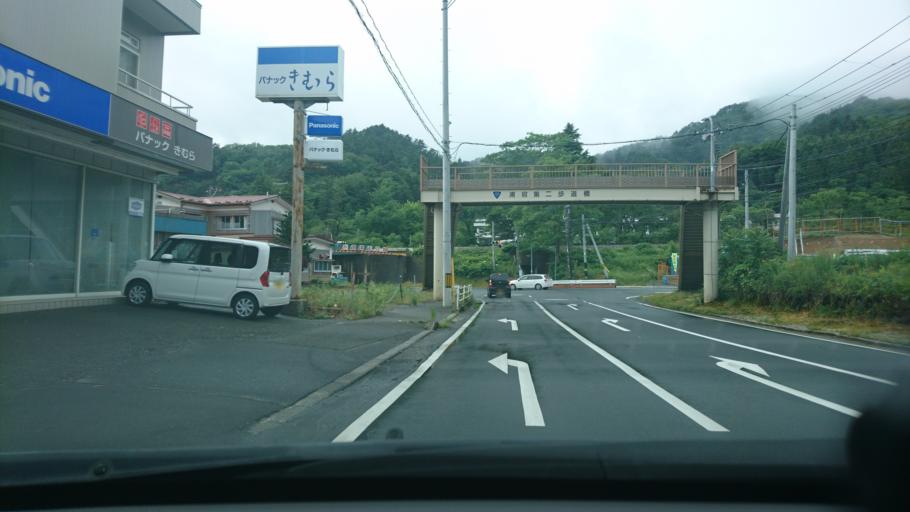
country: JP
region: Miyagi
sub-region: Oshika Gun
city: Onagawa Cho
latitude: 38.4385
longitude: 141.4310
